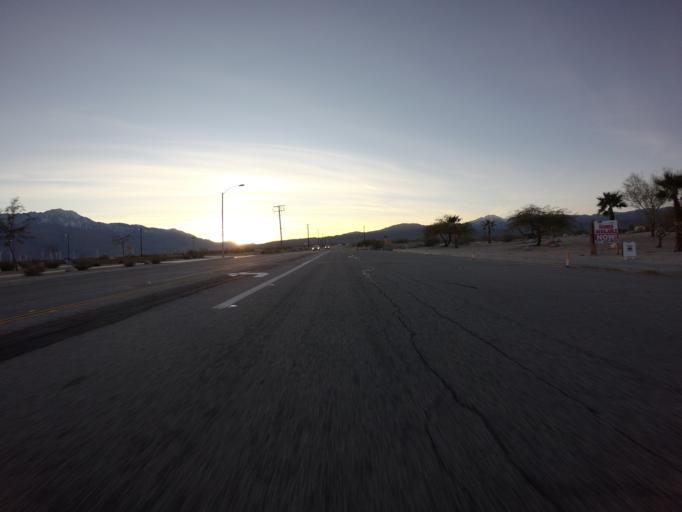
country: US
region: California
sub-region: Riverside County
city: Desert Hot Springs
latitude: 33.9615
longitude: -116.5450
